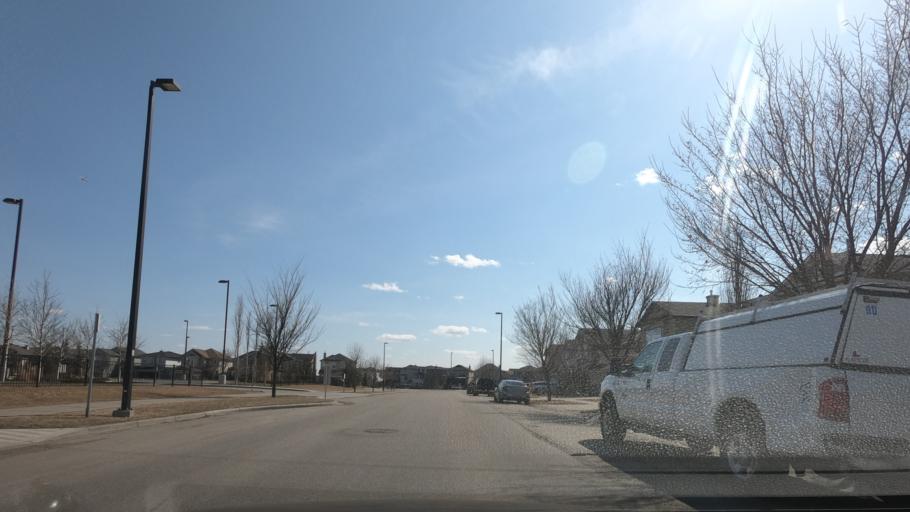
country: CA
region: Alberta
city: Airdrie
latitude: 51.2898
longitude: -114.0426
